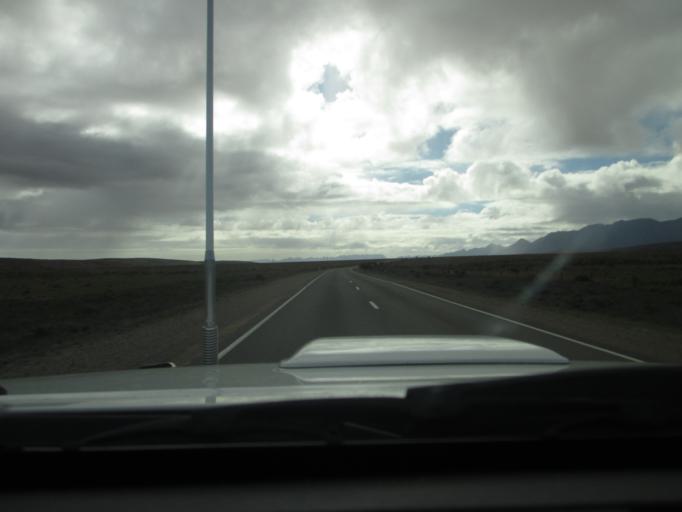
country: AU
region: South Australia
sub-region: Flinders Ranges
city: Quorn
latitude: -31.6033
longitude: 138.4014
